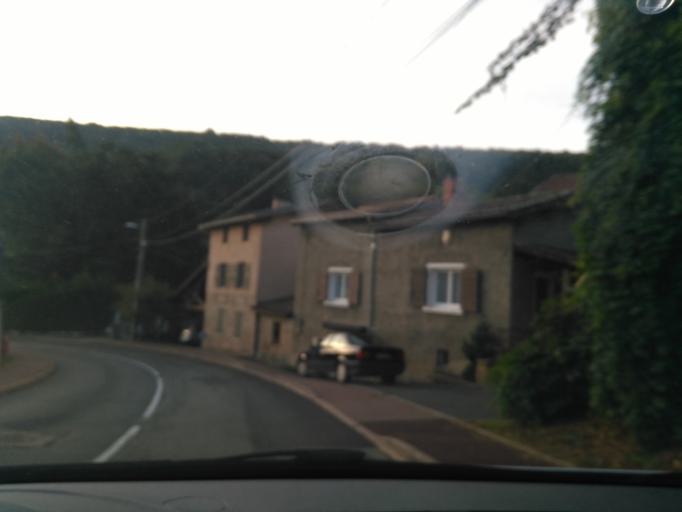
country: FR
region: Rhone-Alpes
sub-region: Departement du Rhone
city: Albigny-sur-Saone
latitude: 45.8545
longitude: 4.8019
